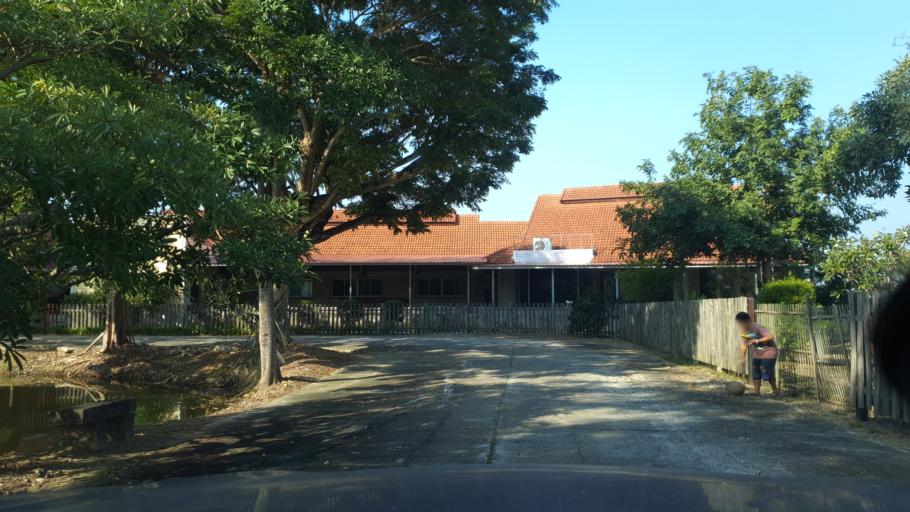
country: TH
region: Chiang Mai
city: Saraphi
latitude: 18.7140
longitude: 98.9963
